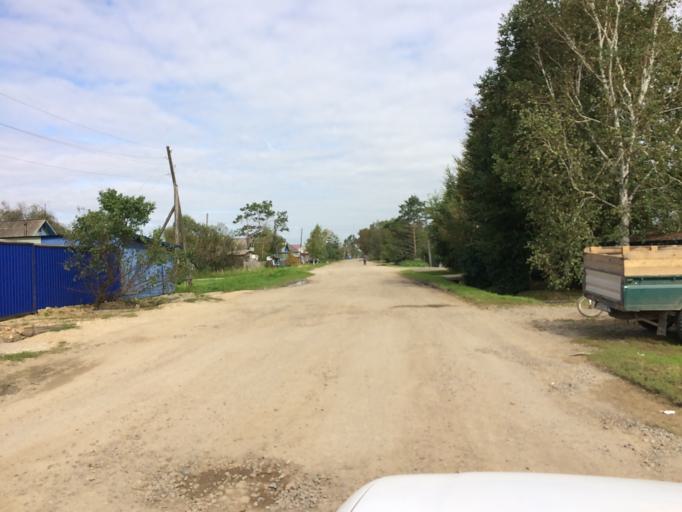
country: RU
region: Primorskiy
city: Dal'nerechensk
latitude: 45.9185
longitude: 133.7221
